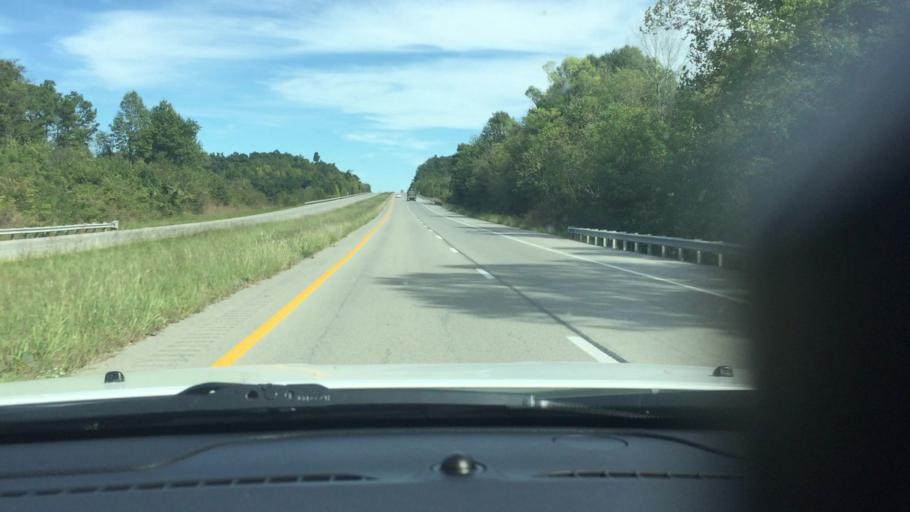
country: US
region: Kentucky
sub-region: Caldwell County
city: Princeton
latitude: 37.1396
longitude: -87.8450
